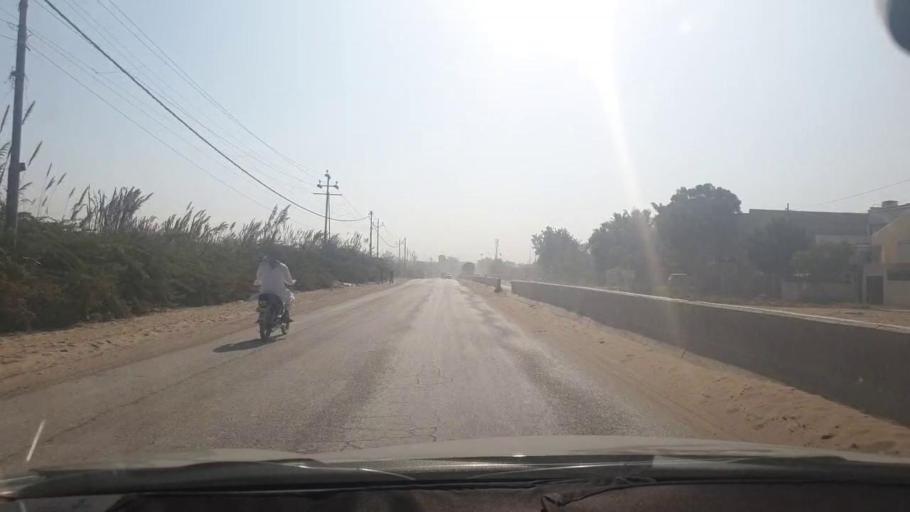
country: PK
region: Sindh
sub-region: Karachi District
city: Karachi
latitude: 25.0038
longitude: 67.0336
